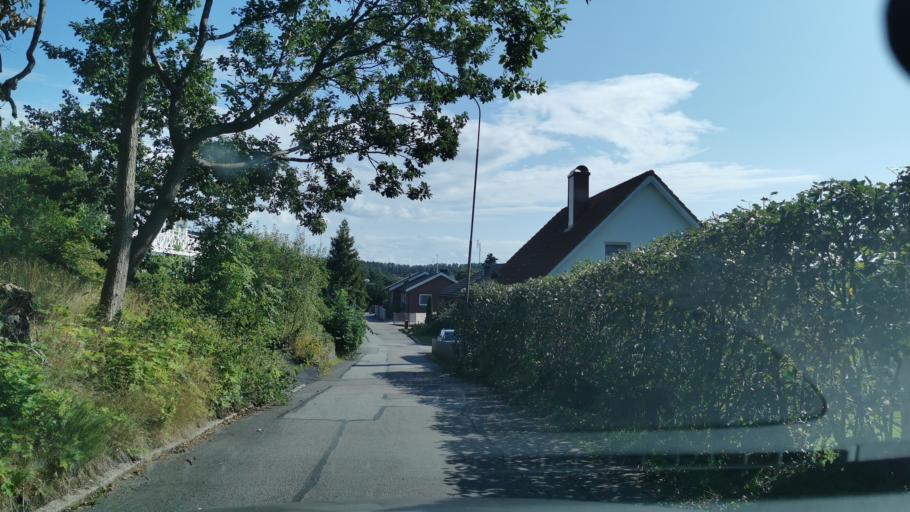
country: SE
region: Vaestra Goetaland
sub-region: Goteborg
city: Majorna
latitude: 57.6398
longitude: 11.9067
